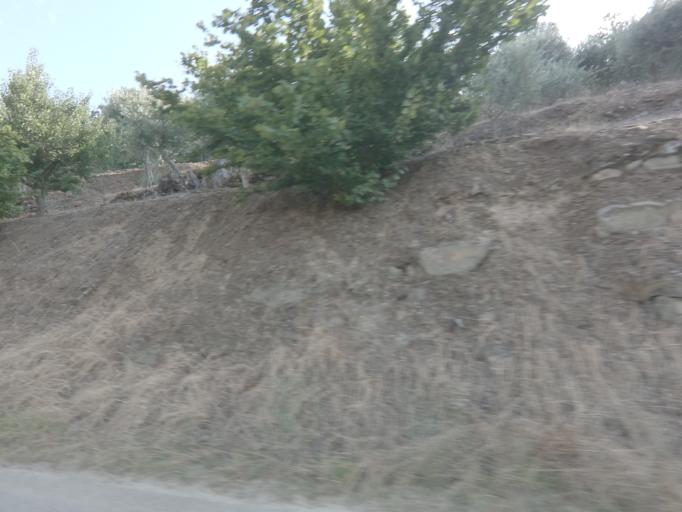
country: PT
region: Viseu
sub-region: Tabuaco
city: Tabuaco
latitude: 41.1306
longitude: -7.5365
